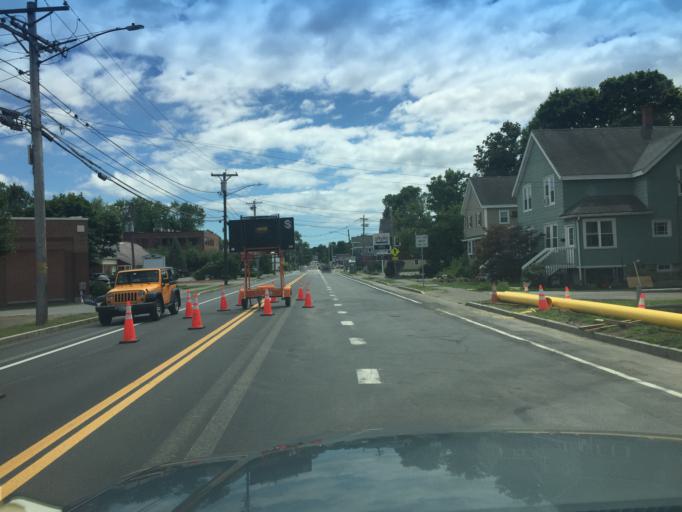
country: US
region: Massachusetts
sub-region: Middlesex County
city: Reading
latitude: 42.5184
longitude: -71.1035
